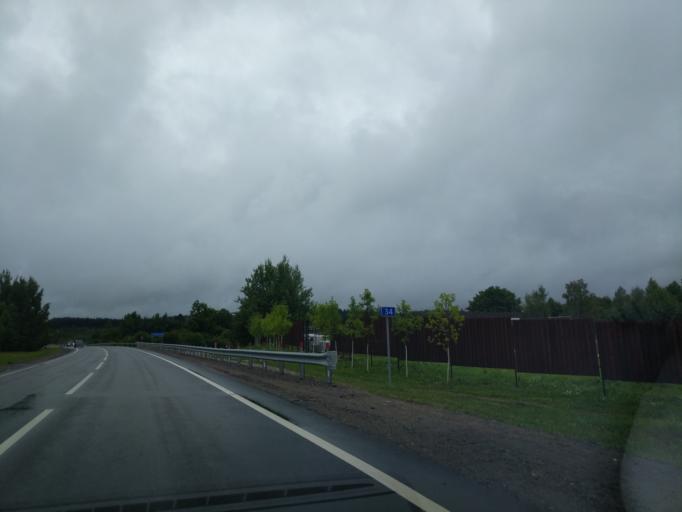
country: BY
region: Minsk
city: Syomkava
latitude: 54.1791
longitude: 27.5004
